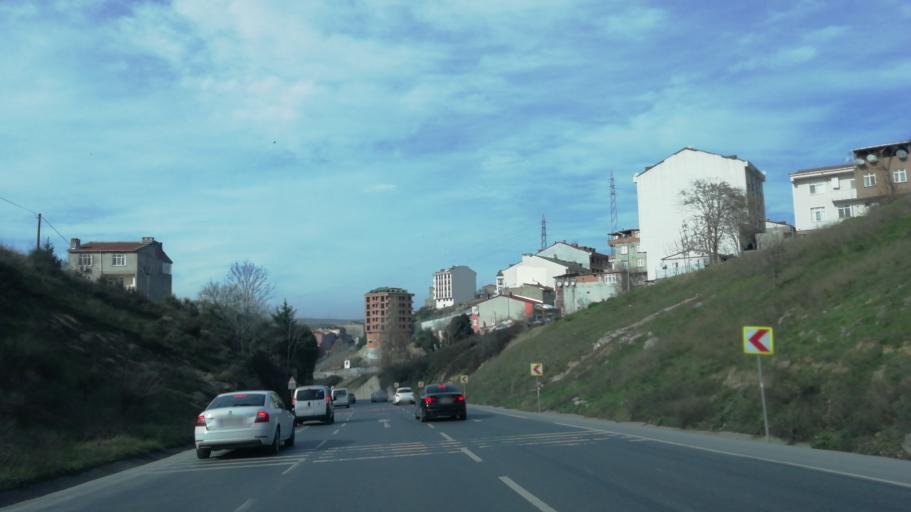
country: TR
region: Istanbul
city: Basaksehir
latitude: 41.0634
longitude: 28.7513
